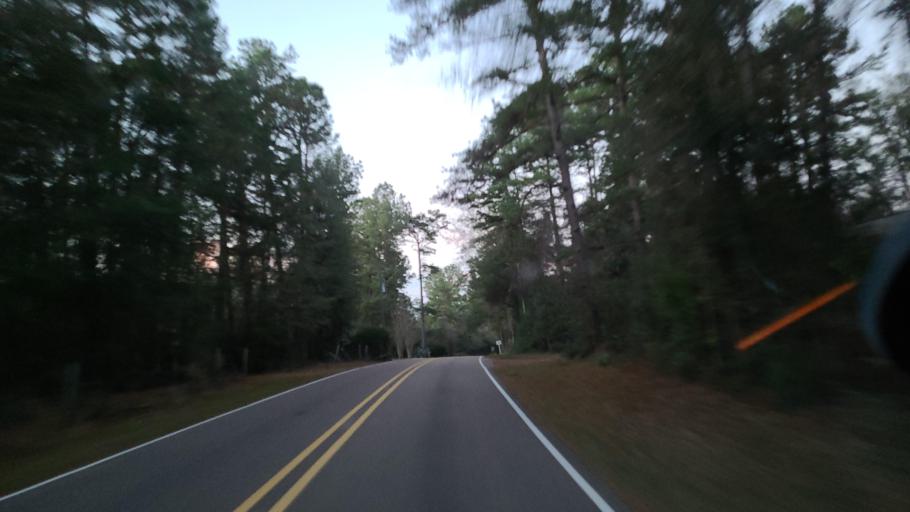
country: US
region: Mississippi
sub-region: Forrest County
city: Hattiesburg
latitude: 31.2382
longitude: -89.2422
